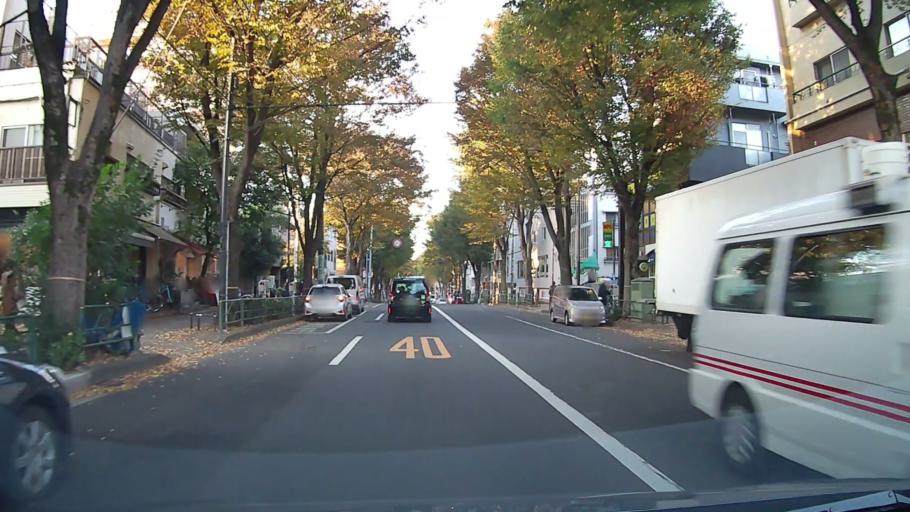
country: JP
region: Tokyo
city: Tokyo
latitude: 35.7075
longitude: 139.6361
